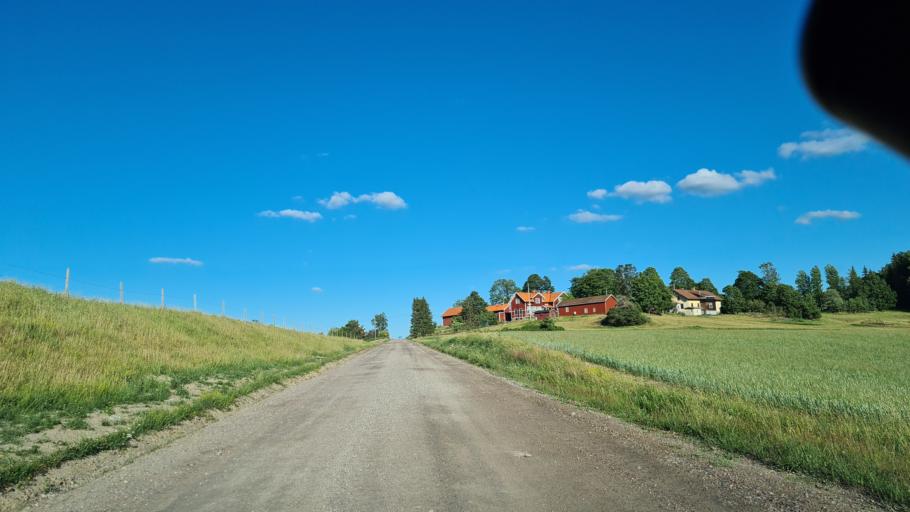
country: SE
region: Soedermanland
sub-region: Nykopings Kommun
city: Nykoping
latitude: 58.9132
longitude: 16.9855
